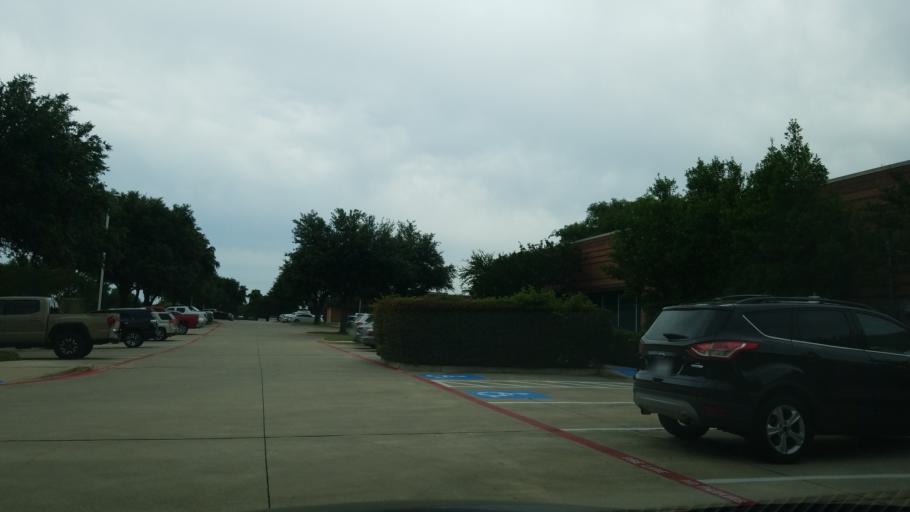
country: US
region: Texas
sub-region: Dallas County
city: Coppell
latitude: 32.8945
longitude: -96.9864
